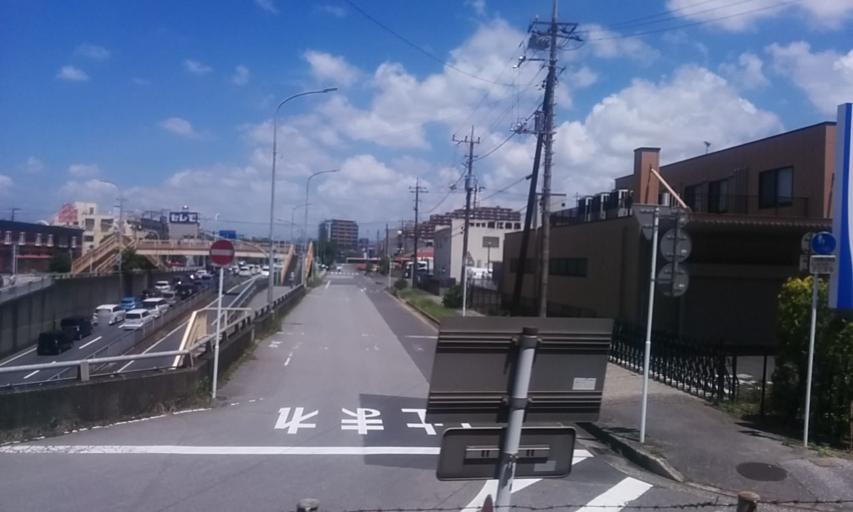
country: JP
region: Chiba
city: Chiba
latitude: 35.5877
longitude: 140.1280
